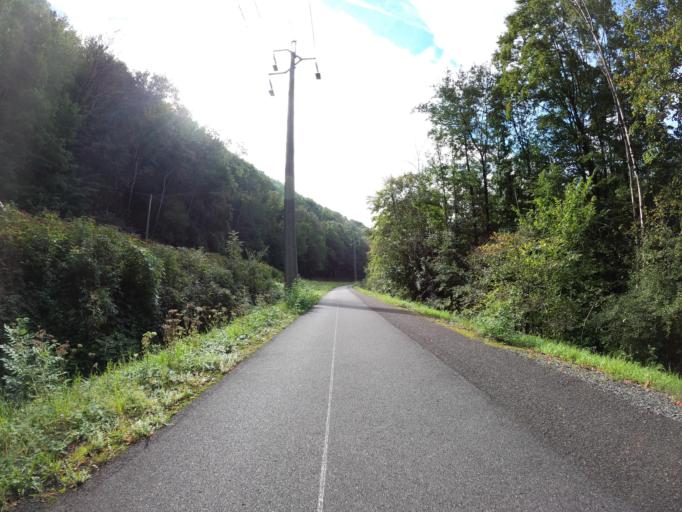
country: FR
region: Midi-Pyrenees
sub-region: Departement des Hautes-Pyrenees
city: Lourdes
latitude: 43.0745
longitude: -0.0405
